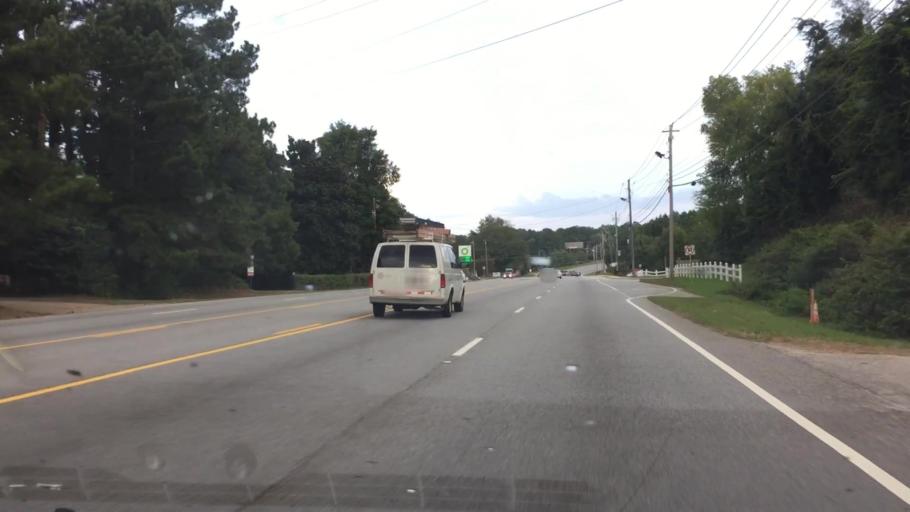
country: US
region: Georgia
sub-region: Clayton County
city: Riverdale
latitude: 33.5418
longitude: -84.3940
